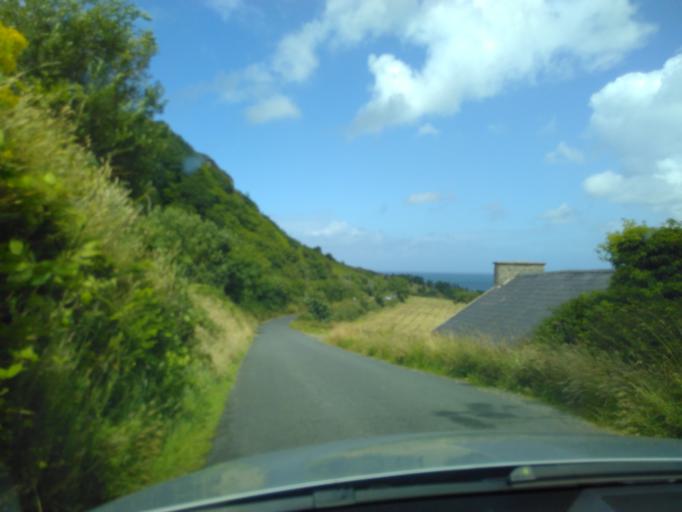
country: IE
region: Ulster
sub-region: County Donegal
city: Ramelton
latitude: 55.2251
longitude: -7.6236
